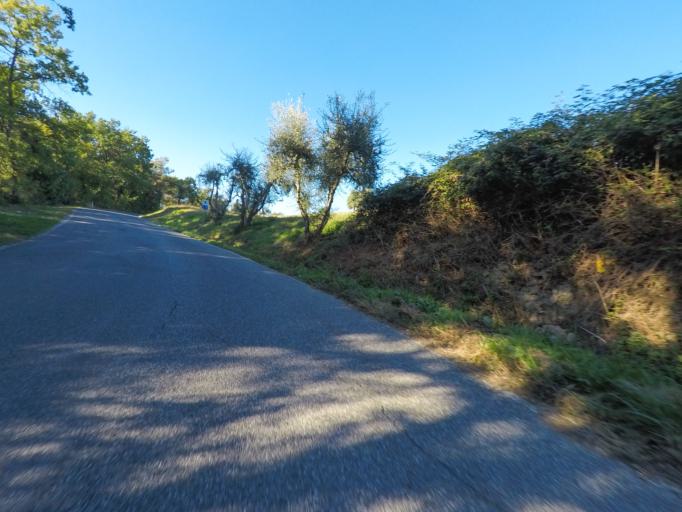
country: IT
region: Tuscany
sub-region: Provincia di Siena
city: Belverde
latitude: 43.3879
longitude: 11.3455
